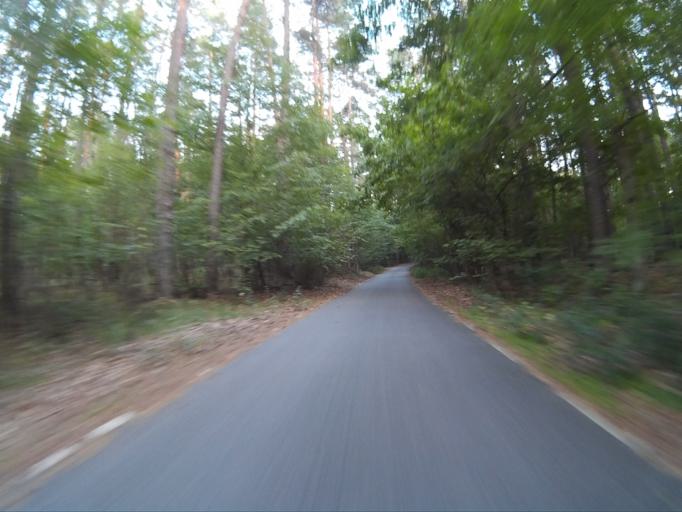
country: PL
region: Kujawsko-Pomorskie
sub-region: Powiat tucholski
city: Tuchola
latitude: 53.6650
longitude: 17.9180
